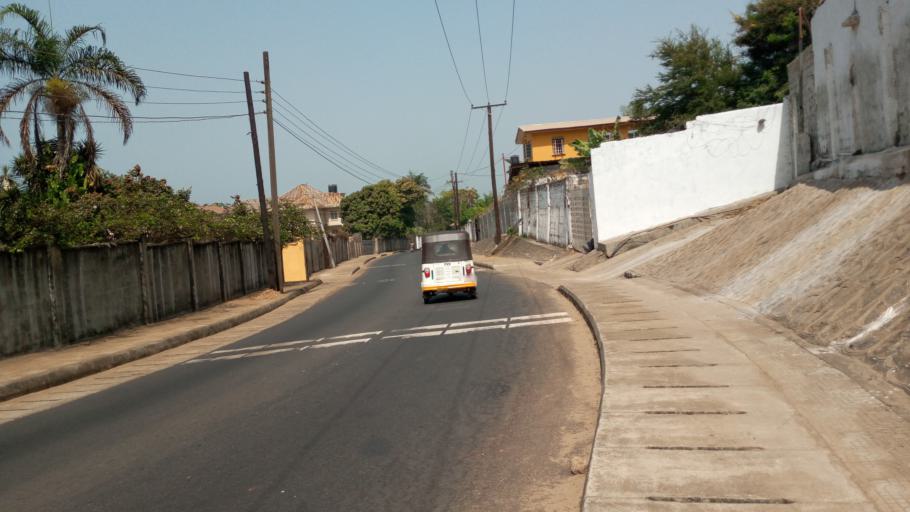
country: SL
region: Western Area
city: Freetown
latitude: 8.4825
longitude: -13.2619
